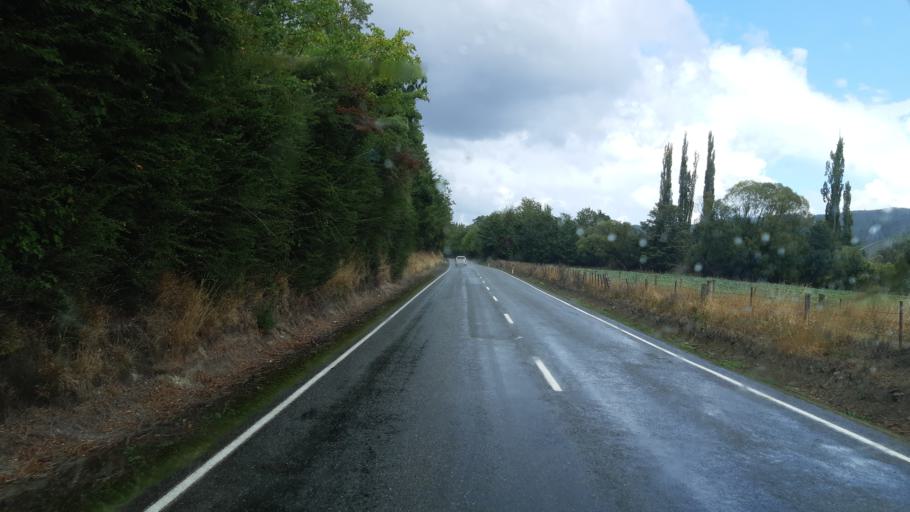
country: NZ
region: Tasman
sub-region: Tasman District
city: Wakefield
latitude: -41.4652
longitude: 172.8400
